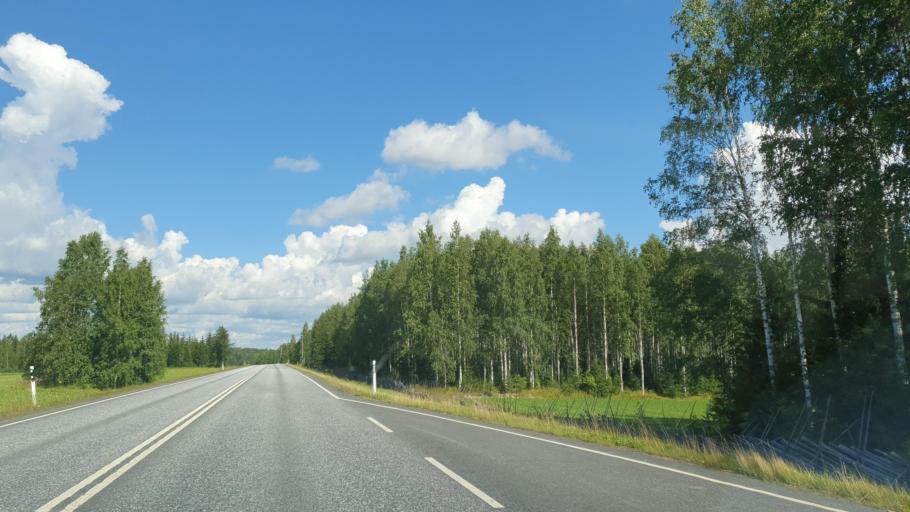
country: FI
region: Northern Savo
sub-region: Ylae-Savo
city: Sonkajaervi
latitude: 63.8088
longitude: 27.4189
